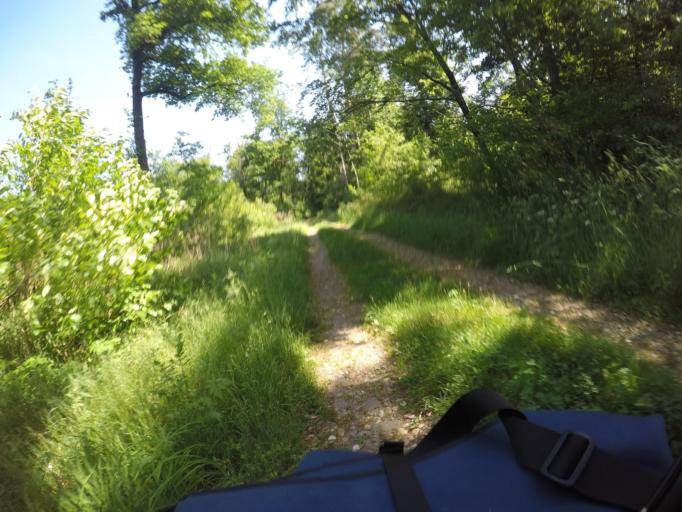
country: DE
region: Baden-Wuerttemberg
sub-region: Karlsruhe Region
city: Rheinstetten
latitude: 48.9435
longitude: 8.3150
